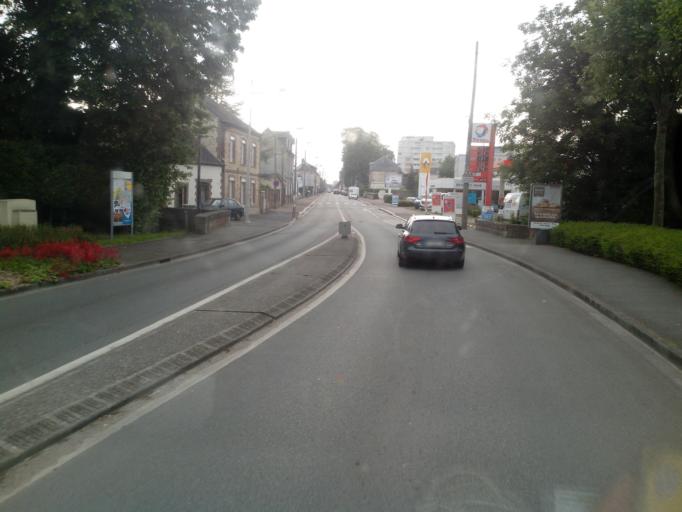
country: FR
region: Haute-Normandie
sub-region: Departement de la Seine-Maritime
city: Fecamp
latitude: 49.7510
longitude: 0.4031
